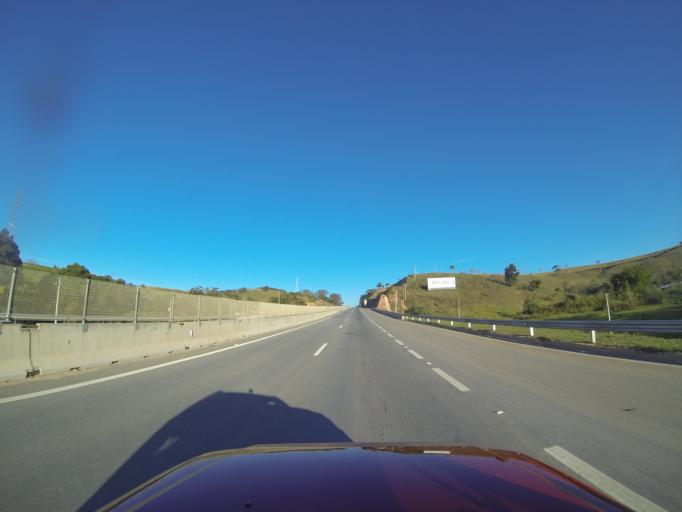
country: BR
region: Sao Paulo
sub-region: Santa Branca
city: Santa Branca
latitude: -23.3174
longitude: -45.7507
